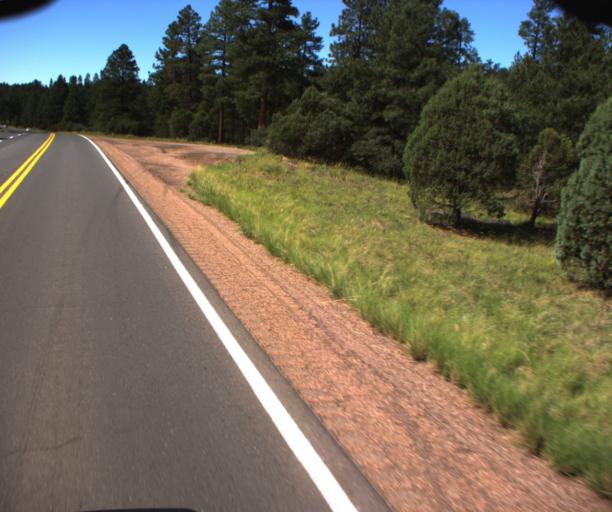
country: US
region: Arizona
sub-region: Navajo County
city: Show Low
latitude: 34.1800
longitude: -110.0956
